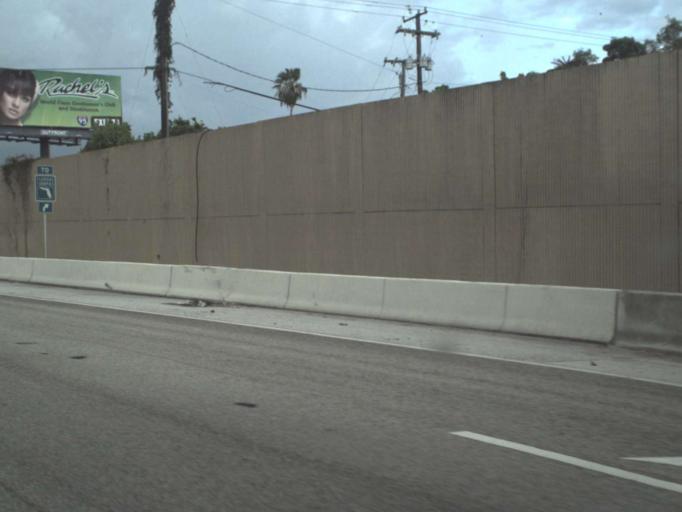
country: US
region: Florida
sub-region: Palm Beach County
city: West Palm Beach
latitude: 26.6984
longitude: -80.0705
